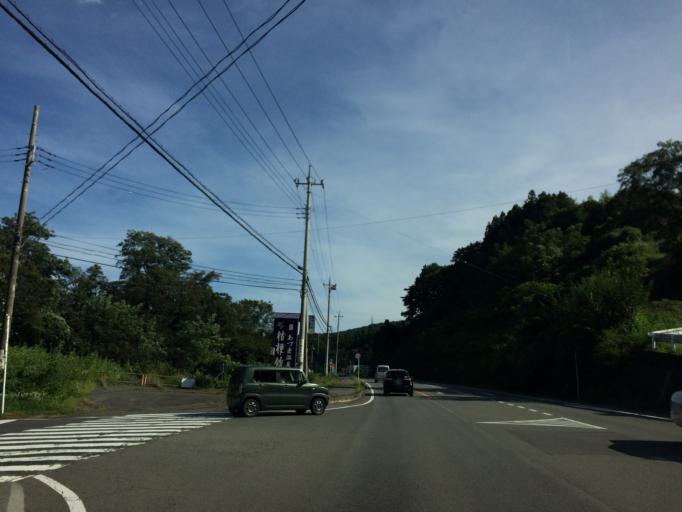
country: JP
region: Gunma
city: Nakanojomachi
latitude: 36.5581
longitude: 138.8928
